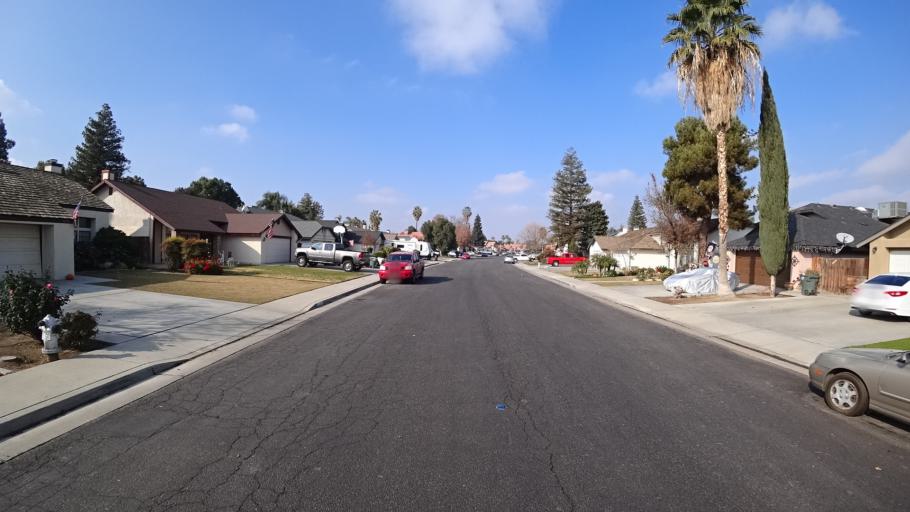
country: US
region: California
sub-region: Kern County
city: Greenacres
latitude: 35.2980
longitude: -119.0872
